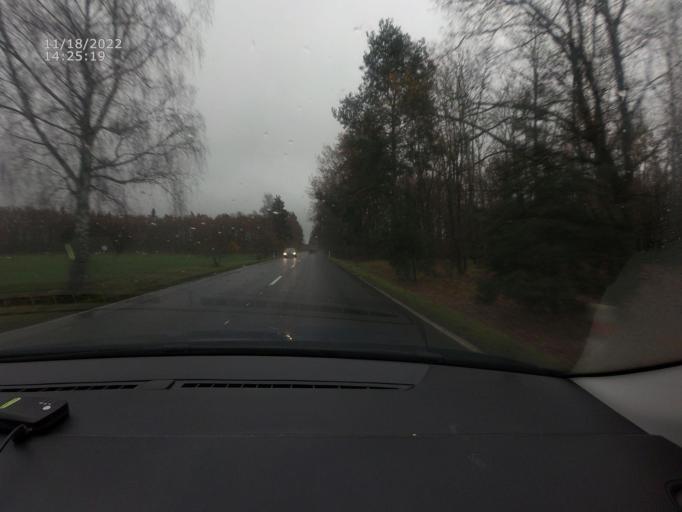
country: CZ
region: Jihocesky
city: Cimelice
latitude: 49.4347
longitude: 14.1514
